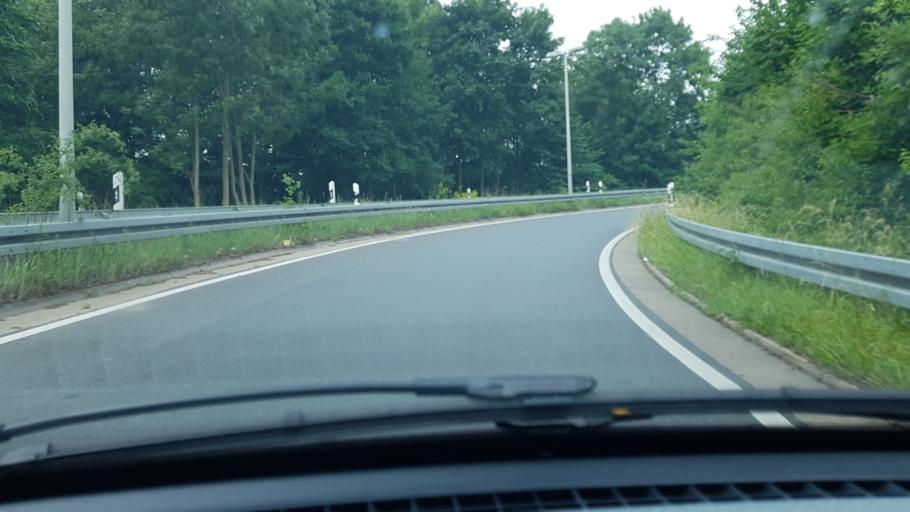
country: DE
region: Lower Saxony
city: Braunschweig
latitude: 52.2458
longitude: 10.5066
